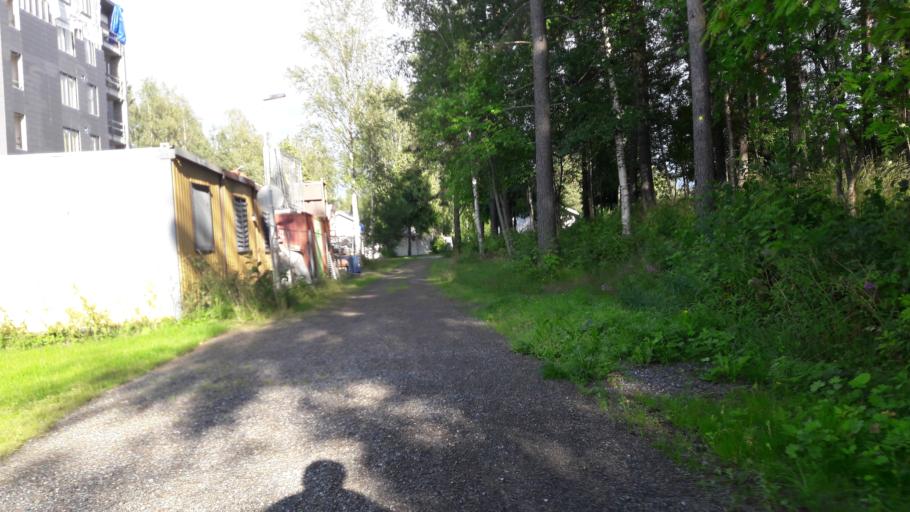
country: FI
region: North Karelia
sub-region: Joensuu
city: Joensuu
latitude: 62.6040
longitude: 29.8028
